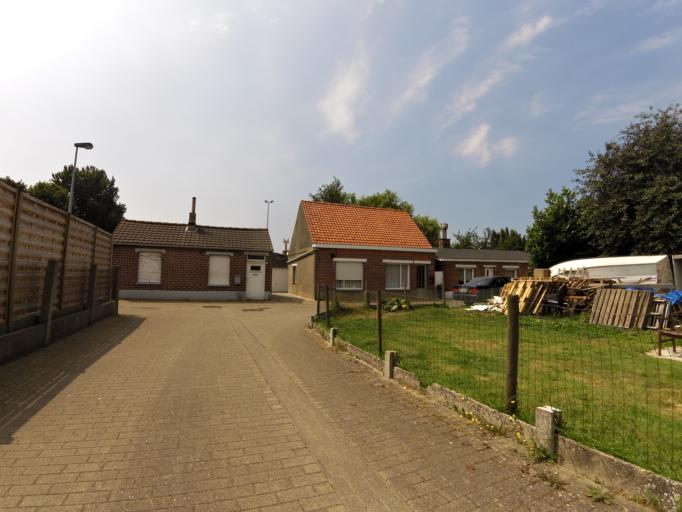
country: BE
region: Flanders
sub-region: Provincie West-Vlaanderen
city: Oudenburg
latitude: 51.1801
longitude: 3.0100
